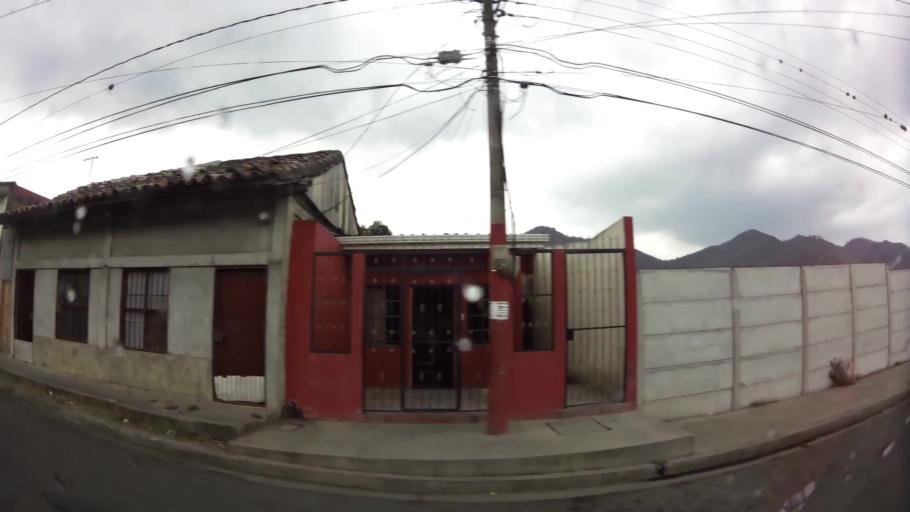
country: NI
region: Jinotega
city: Jinotega
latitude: 13.0919
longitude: -86.0002
